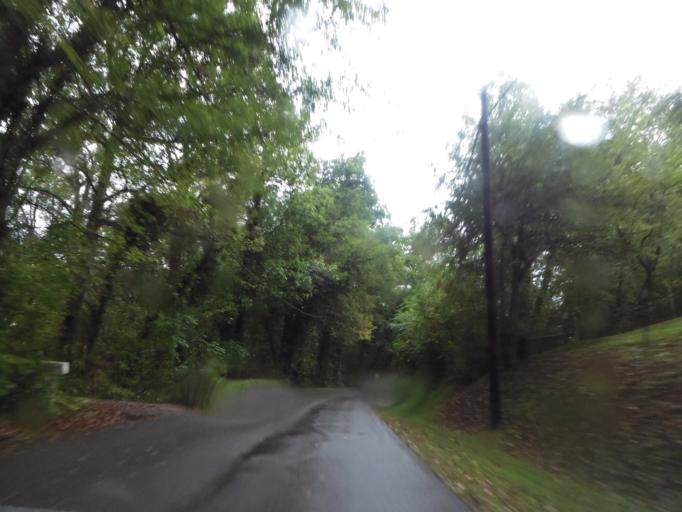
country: US
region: Tennessee
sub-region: Blount County
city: Eagleton Village
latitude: 35.8194
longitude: -83.9436
